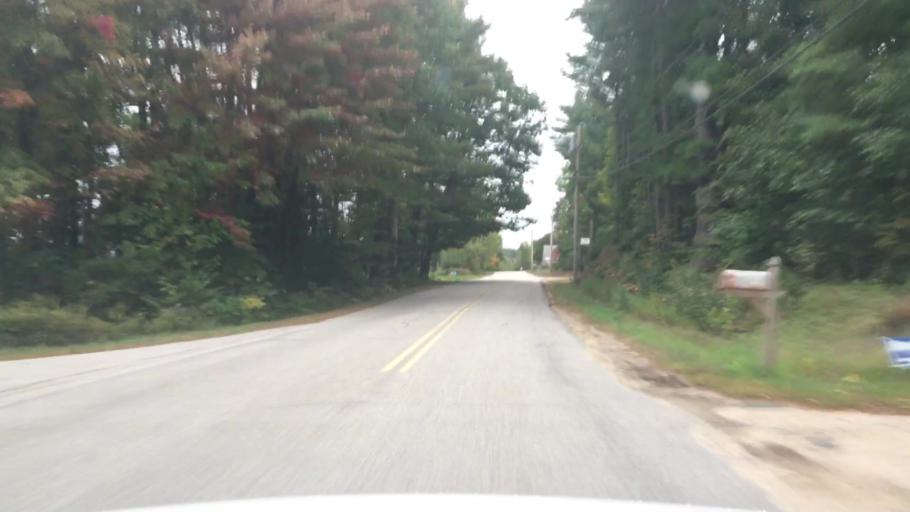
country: US
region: Maine
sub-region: York County
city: Buxton
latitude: 43.6439
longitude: -70.5248
